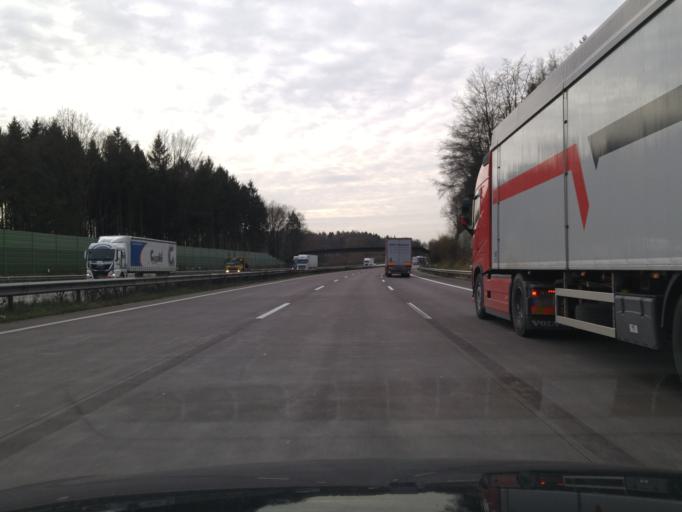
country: DE
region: Schleswig-Holstein
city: Grosshansdorf
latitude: 53.6563
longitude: 10.2961
